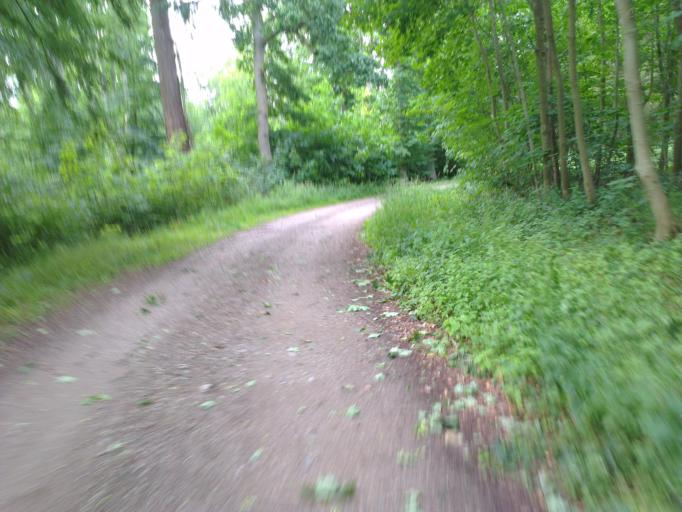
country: DK
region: Capital Region
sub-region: Frederikssund Kommune
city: Jaegerspris
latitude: 55.8808
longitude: 11.9868
